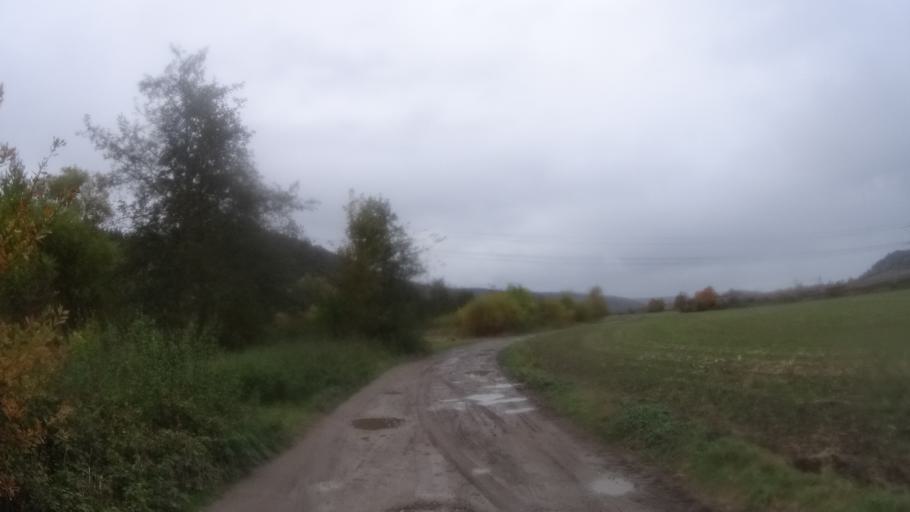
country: DE
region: Thuringia
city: Grosseutersdorf
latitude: 50.7841
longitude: 11.5646
